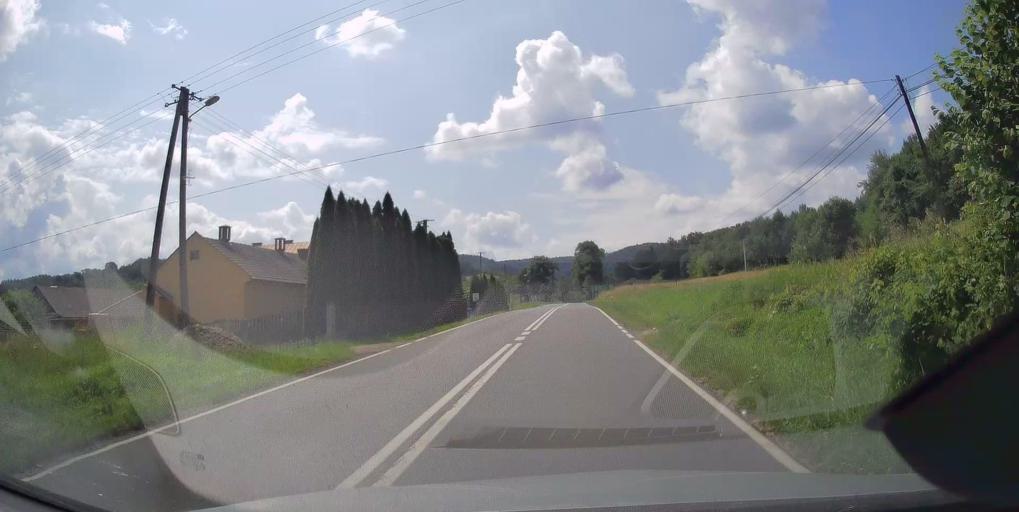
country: PL
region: Lesser Poland Voivodeship
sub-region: Powiat tarnowski
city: Zakliczyn
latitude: 49.8353
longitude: 20.8116
